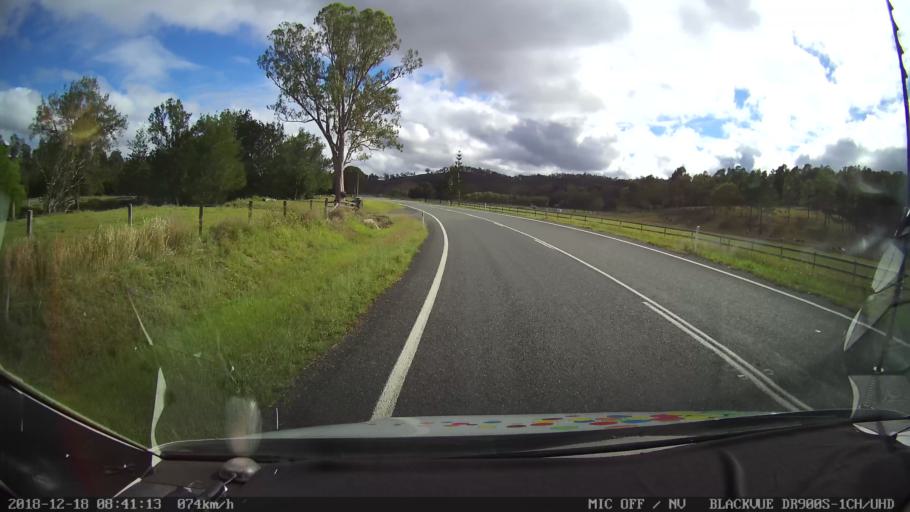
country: AU
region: Queensland
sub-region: Logan
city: Cedar Vale
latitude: -28.2384
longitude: 152.8554
